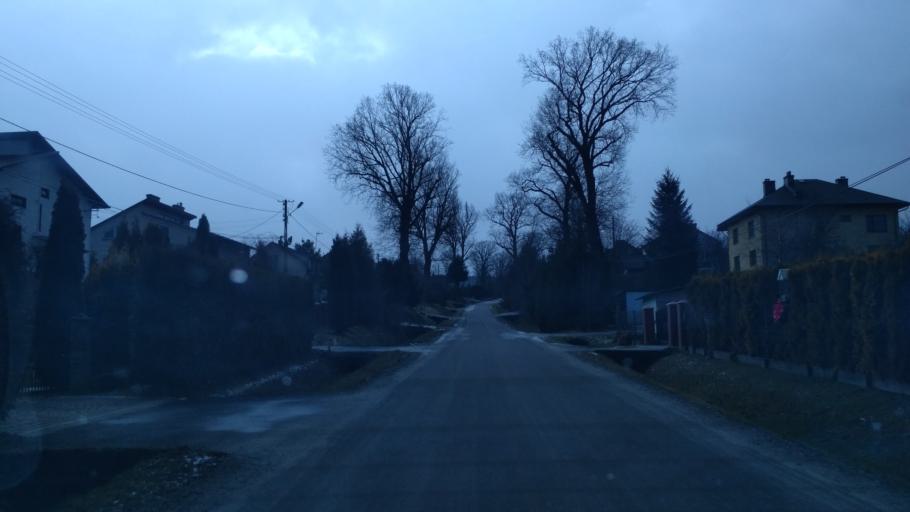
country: PL
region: Subcarpathian Voivodeship
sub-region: Powiat rzeszowski
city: Hyzne
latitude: 49.9065
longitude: 22.1971
